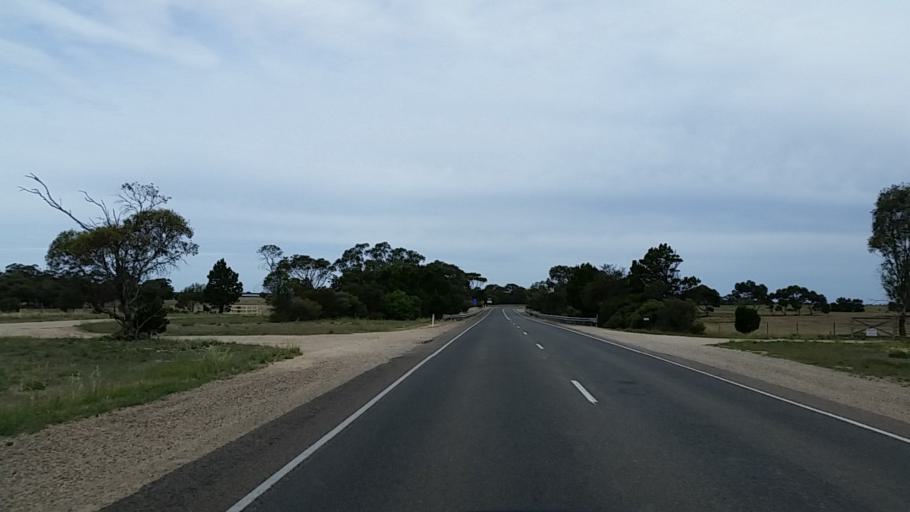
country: AU
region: South Australia
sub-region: Murray Bridge
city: Murray Bridge
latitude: -35.1256
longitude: 139.3200
